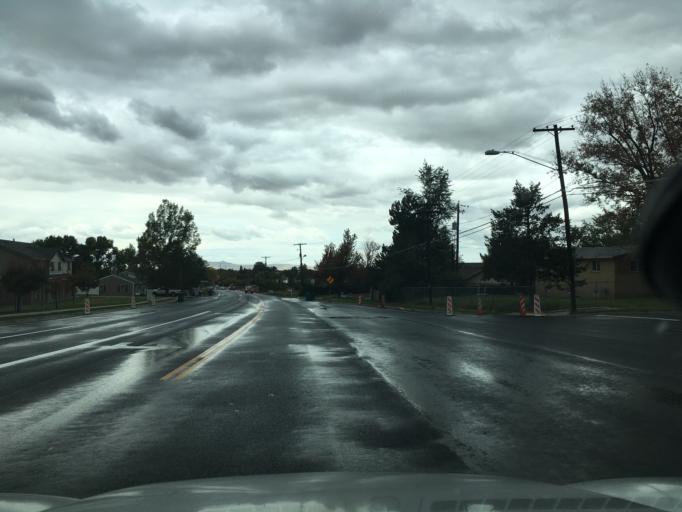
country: US
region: Utah
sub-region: Davis County
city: Kaysville
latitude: 41.0625
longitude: -111.9407
